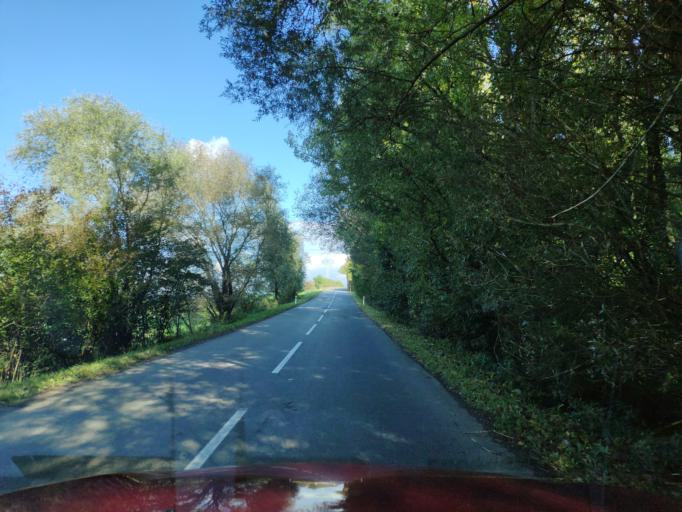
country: SK
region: Presovsky
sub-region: Okres Presov
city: Presov
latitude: 48.9023
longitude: 21.2623
